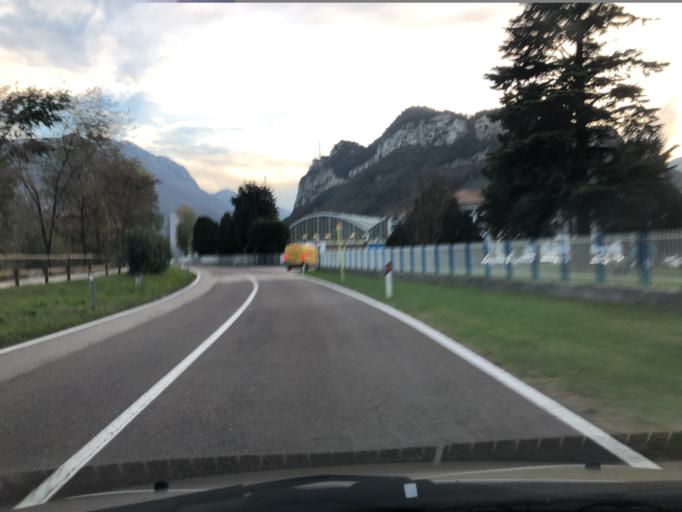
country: IT
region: Trentino-Alto Adige
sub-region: Provincia di Trento
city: Arco
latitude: 45.9000
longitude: 10.8802
